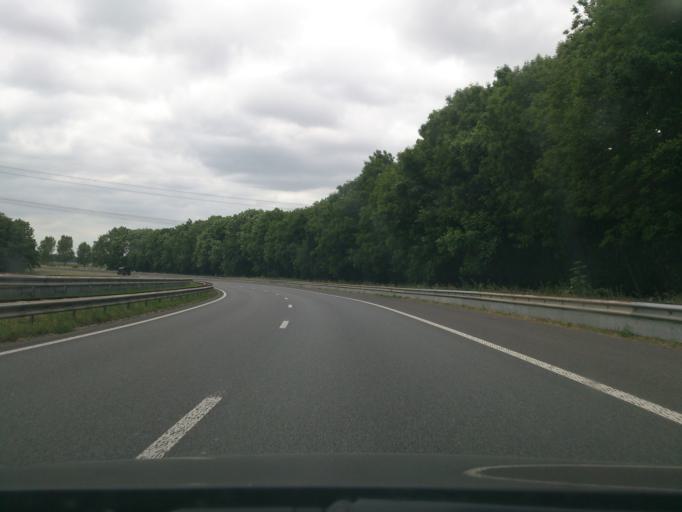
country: NL
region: Gelderland
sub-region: Gemeente Wijchen
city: Bergharen
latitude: 51.8144
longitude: 5.6777
